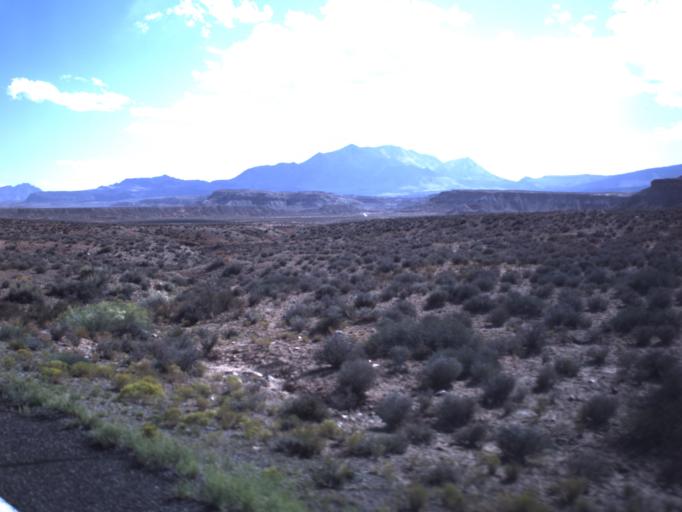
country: US
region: Utah
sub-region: Wayne County
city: Loa
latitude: 38.0916
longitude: -110.6185
